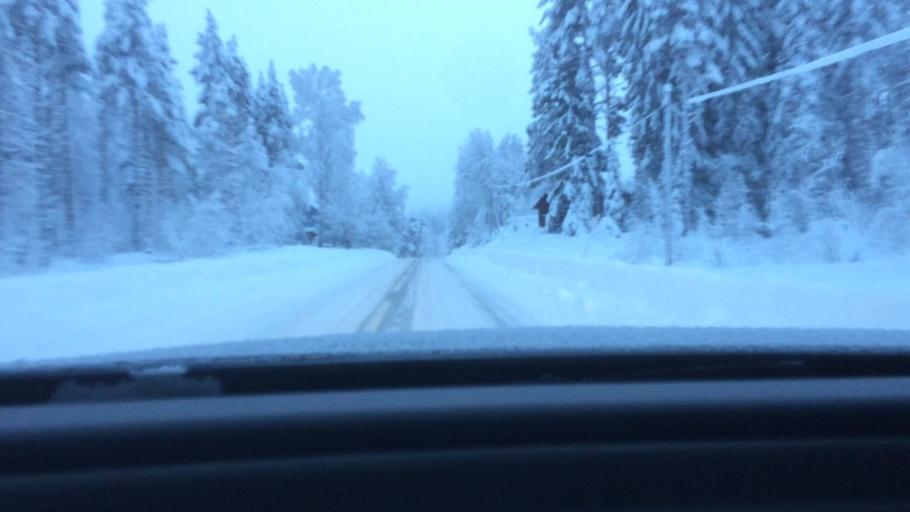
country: SE
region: Gaevleborg
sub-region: Ljusdals Kommun
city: Farila
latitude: 61.7653
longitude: 15.1532
